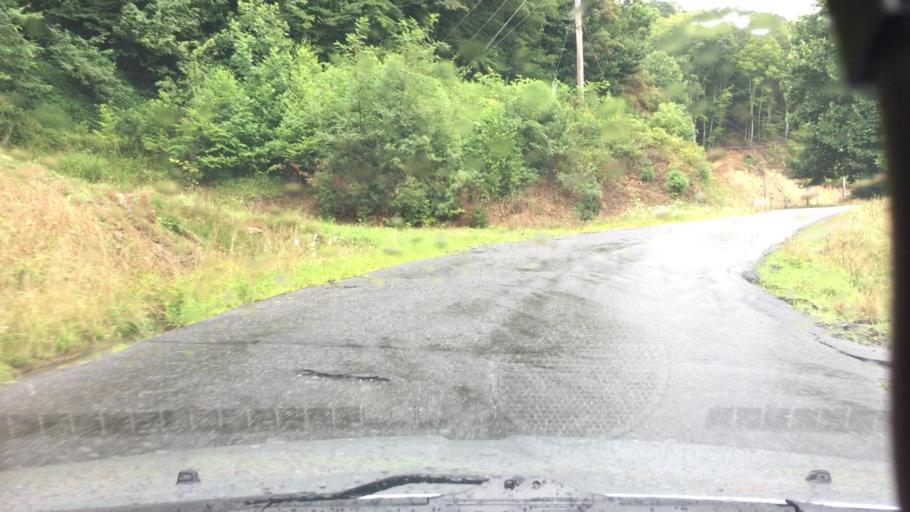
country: US
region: North Carolina
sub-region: Madison County
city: Mars Hill
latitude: 35.9559
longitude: -82.5101
